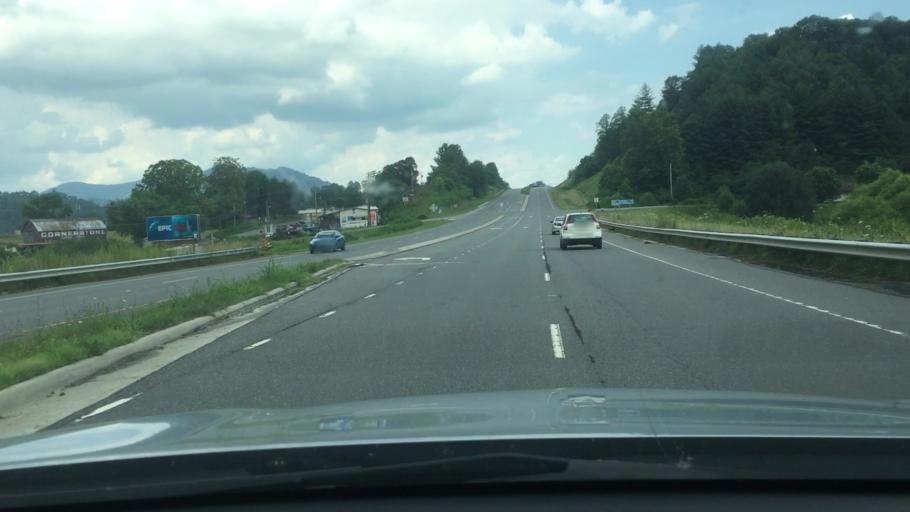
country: US
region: North Carolina
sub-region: Yancey County
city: Burnsville
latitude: 35.9107
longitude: -82.3830
